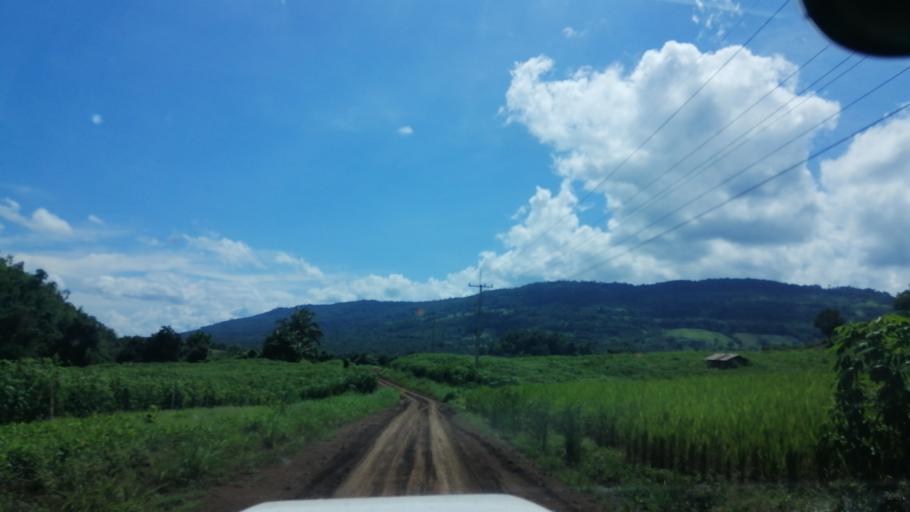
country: TH
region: Uttaradit
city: Ban Khok
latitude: 18.0946
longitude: 101.2481
